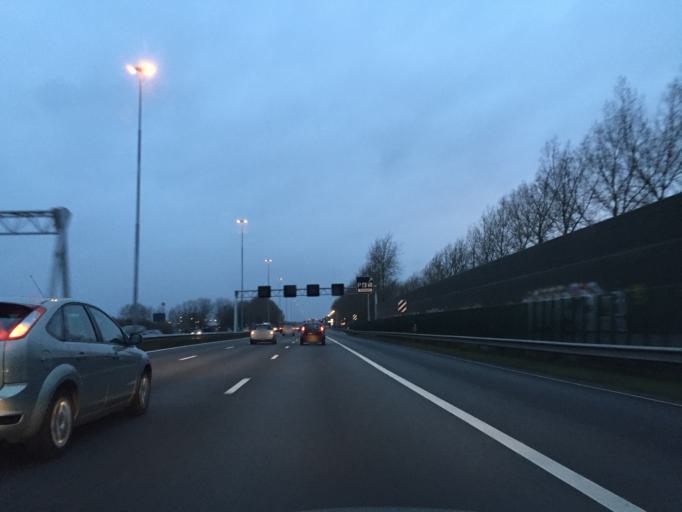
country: NL
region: South Holland
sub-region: Gemeente Delft
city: Delft
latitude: 51.9785
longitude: 4.3969
